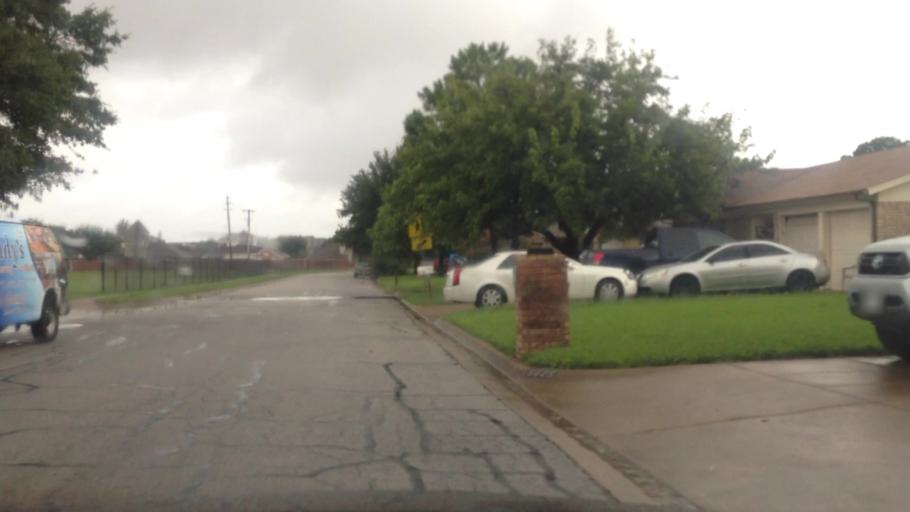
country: US
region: Texas
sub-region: Tarrant County
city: North Richland Hills
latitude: 32.8493
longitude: -97.2068
